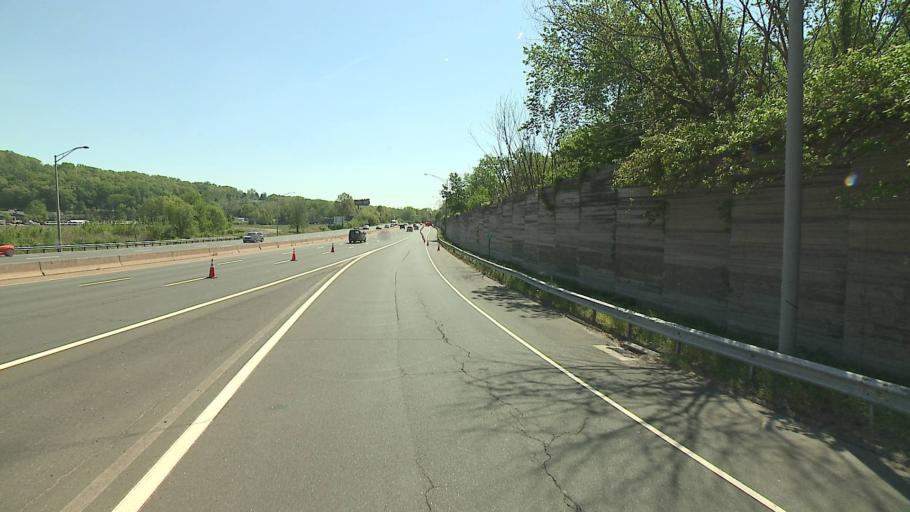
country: US
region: Connecticut
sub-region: Fairfield County
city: Danbury
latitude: 41.3898
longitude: -73.5129
